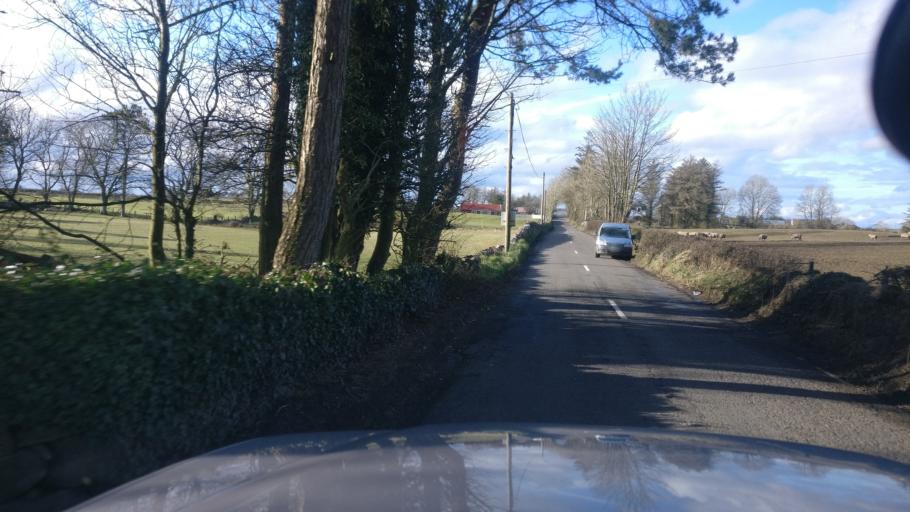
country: IE
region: Connaught
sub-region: County Galway
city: Loughrea
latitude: 53.1989
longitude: -8.3992
